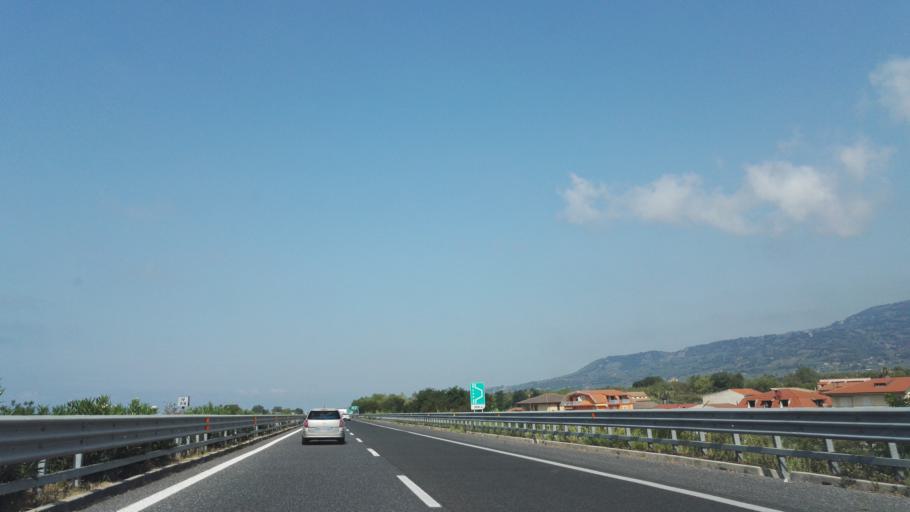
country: IT
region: Calabria
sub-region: Provincia di Catanzaro
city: Santa Eufemia Lamezia
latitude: 38.9267
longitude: 16.2481
